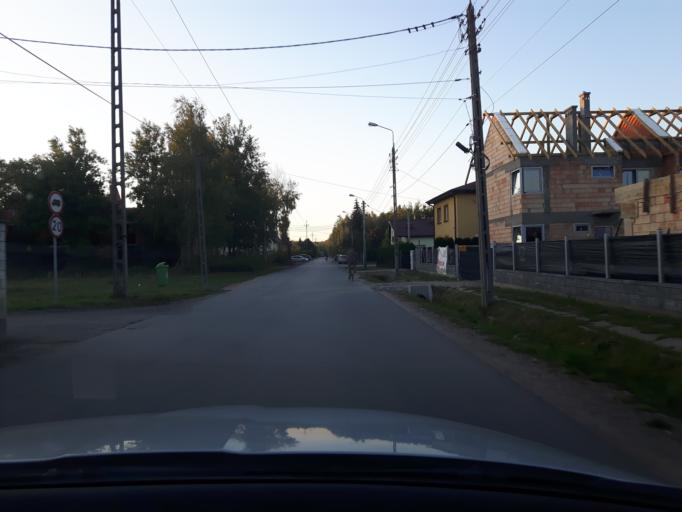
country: PL
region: Masovian Voivodeship
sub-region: Powiat wolominski
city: Kobylka
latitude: 52.3398
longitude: 21.1802
